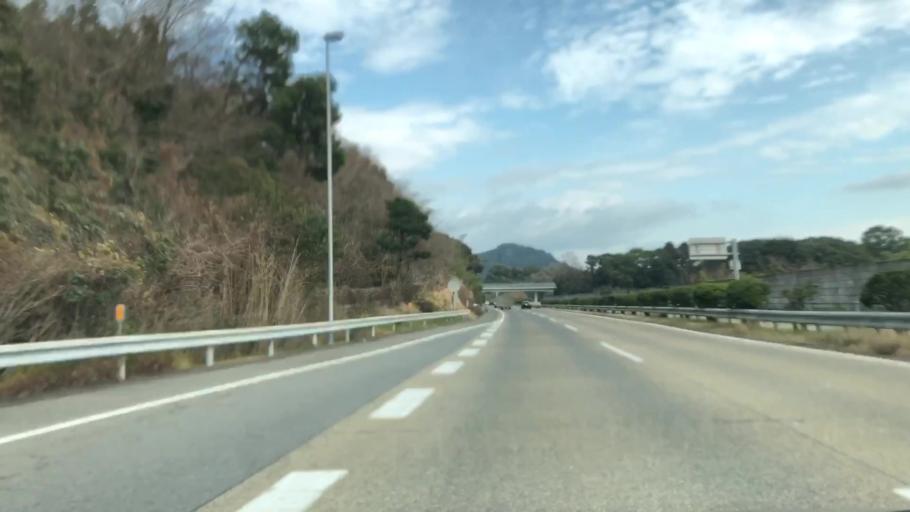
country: JP
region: Saga Prefecture
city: Kanzakimachi-kanzaki
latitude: 33.3301
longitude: 130.3155
